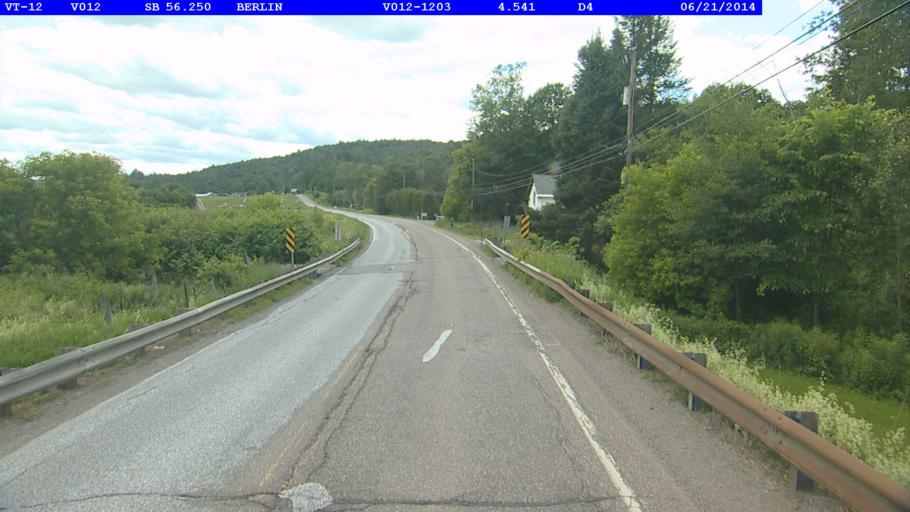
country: US
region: Vermont
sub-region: Washington County
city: Montpelier
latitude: 44.2295
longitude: -72.6151
